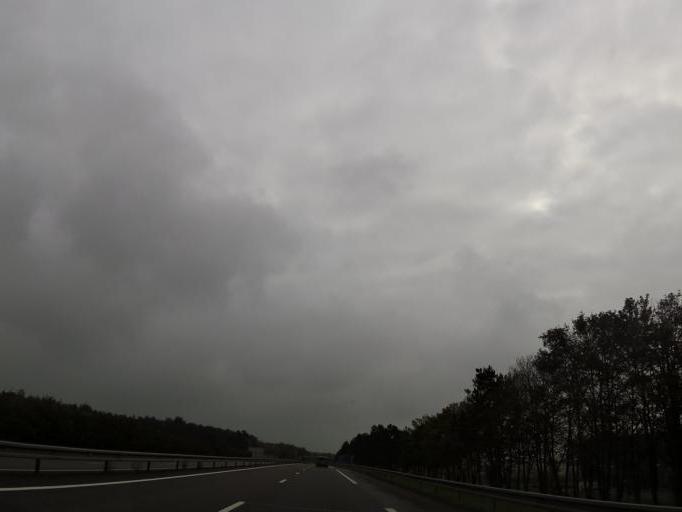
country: FR
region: Champagne-Ardenne
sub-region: Departement de la Marne
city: Fagnieres
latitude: 49.0406
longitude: 4.3343
